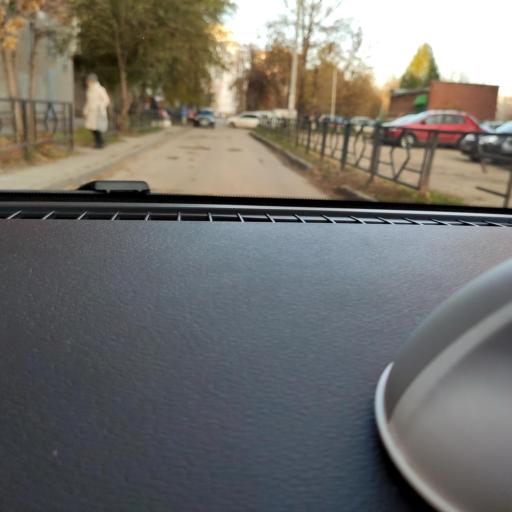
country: RU
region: Samara
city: Samara
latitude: 53.2567
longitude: 50.2358
